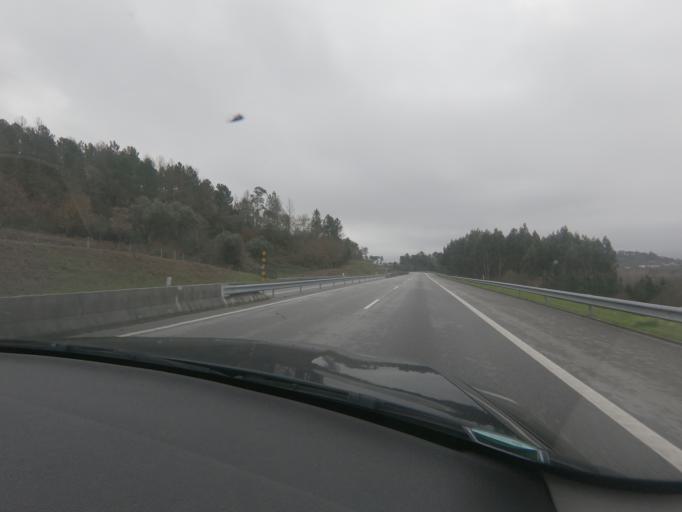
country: PT
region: Viseu
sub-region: Viseu
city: Abraveses
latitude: 40.6517
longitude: -7.9669
